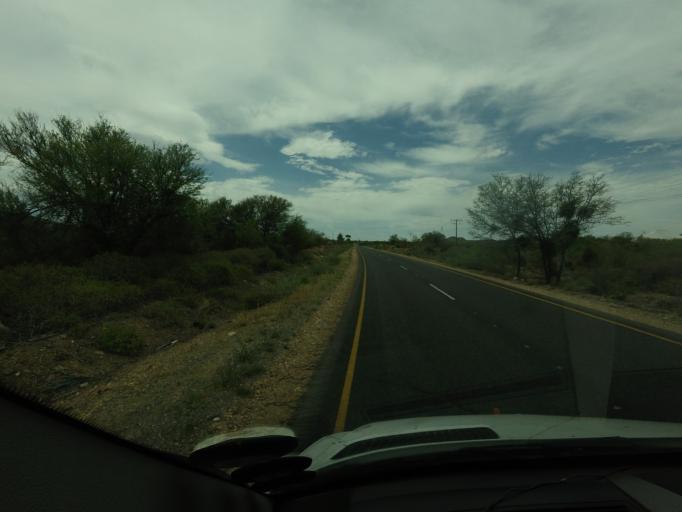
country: ZA
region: Western Cape
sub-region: Overberg District Municipality
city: Swellendam
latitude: -33.8506
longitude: 20.8511
